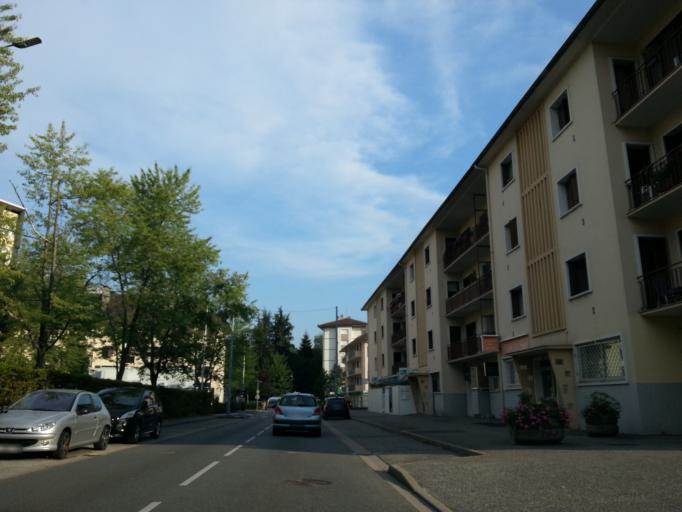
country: FR
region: Rhone-Alpes
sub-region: Departement de la Haute-Savoie
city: Annecy-le-Vieux
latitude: 45.9116
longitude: 6.1443
